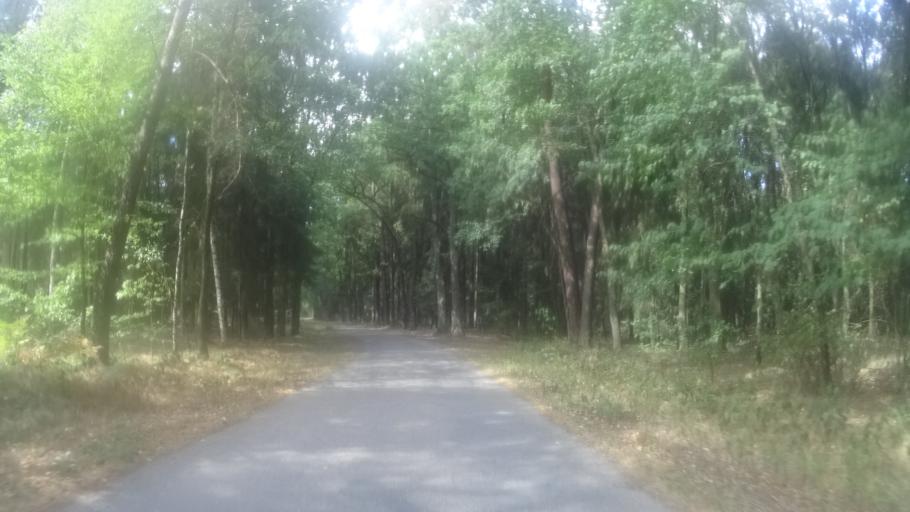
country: CZ
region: Pardubicky
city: Horni Jeleni
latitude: 50.0495
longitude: 16.1558
